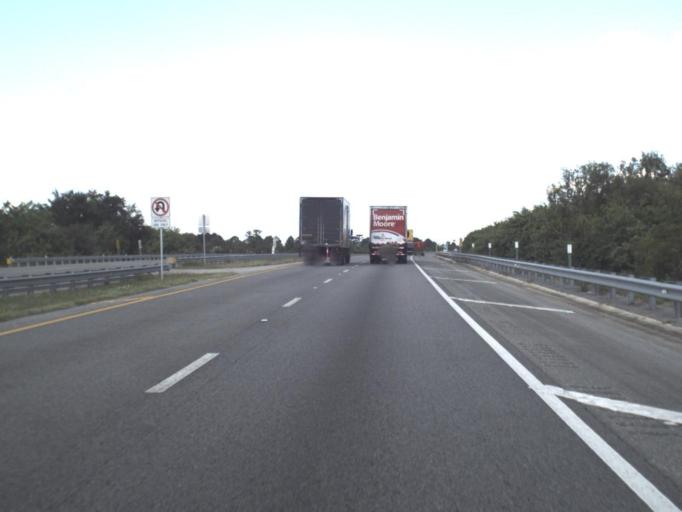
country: US
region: Florida
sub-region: Indian River County
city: Fellsmere
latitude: 27.8078
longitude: -80.9991
